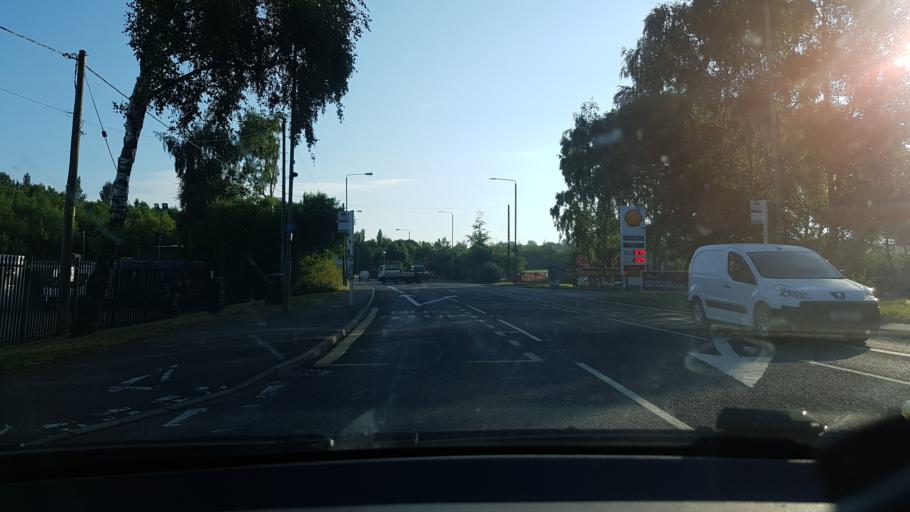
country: GB
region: England
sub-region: Nottinghamshire
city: Awsworth
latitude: 52.9974
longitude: -1.2812
